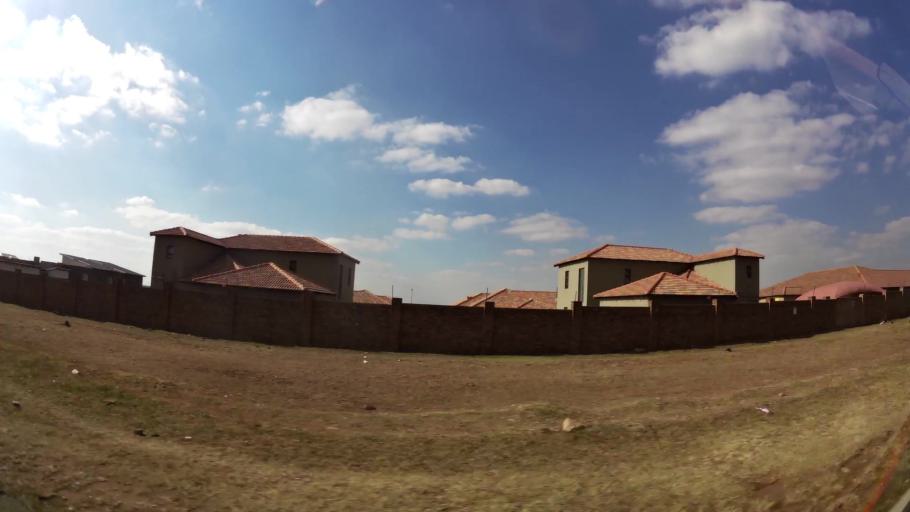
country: ZA
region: Gauteng
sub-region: West Rand District Municipality
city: Krugersdorp
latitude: -26.0621
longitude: 27.7593
